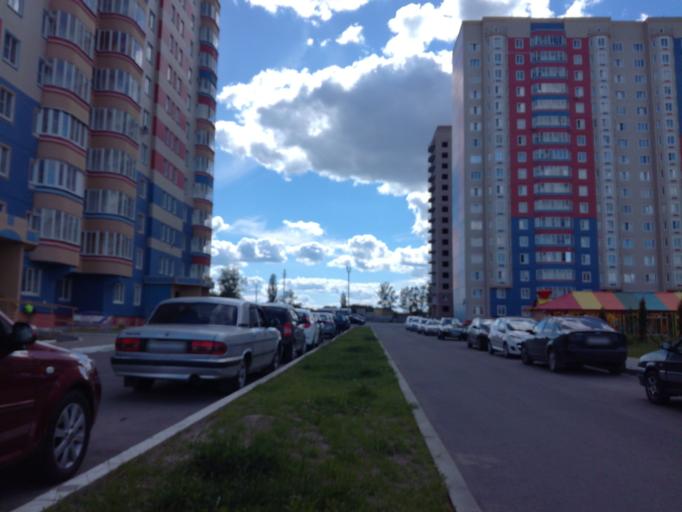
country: RU
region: Kursk
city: Kursk
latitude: 51.8144
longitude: 36.1668
